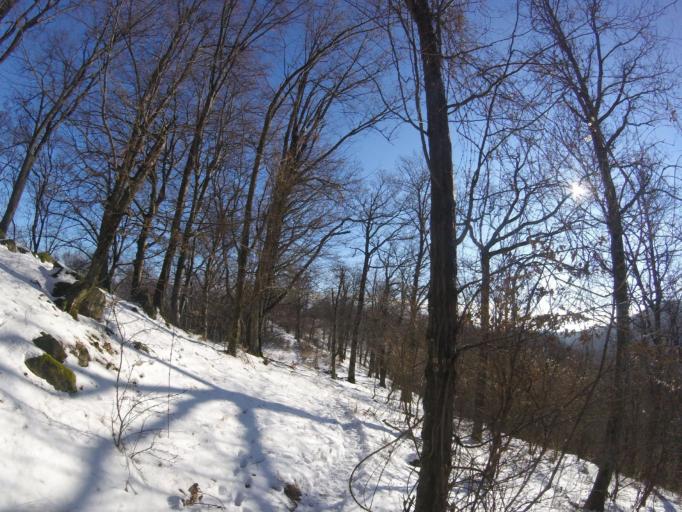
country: SK
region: Nitriansky
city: Sahy
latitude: 47.9672
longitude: 18.8813
